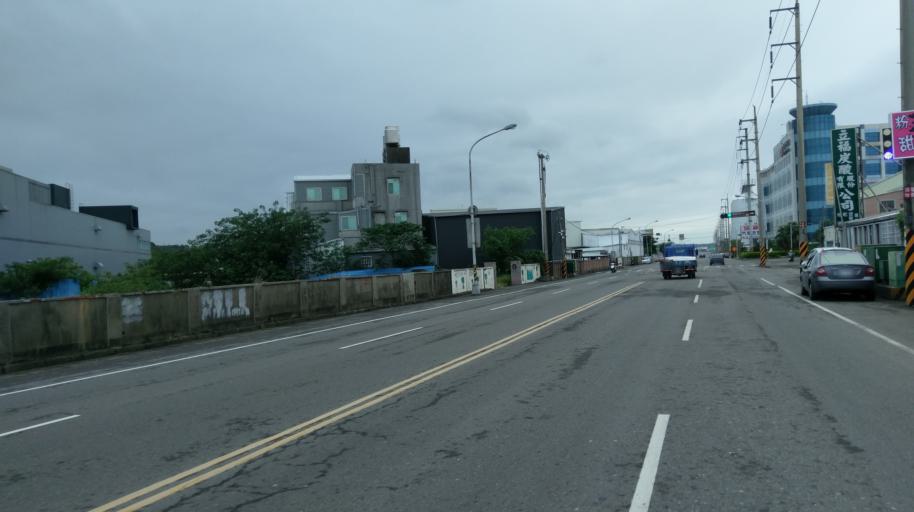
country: TW
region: Taiwan
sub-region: Miaoli
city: Miaoli
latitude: 24.6737
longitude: 120.8907
